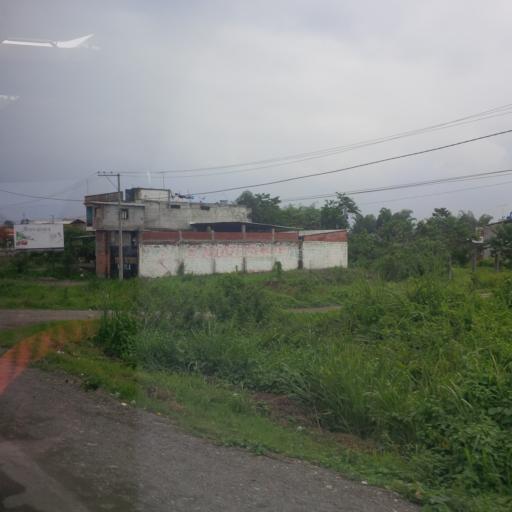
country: EC
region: Canar
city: La Troncal
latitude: -2.3375
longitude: -79.3919
